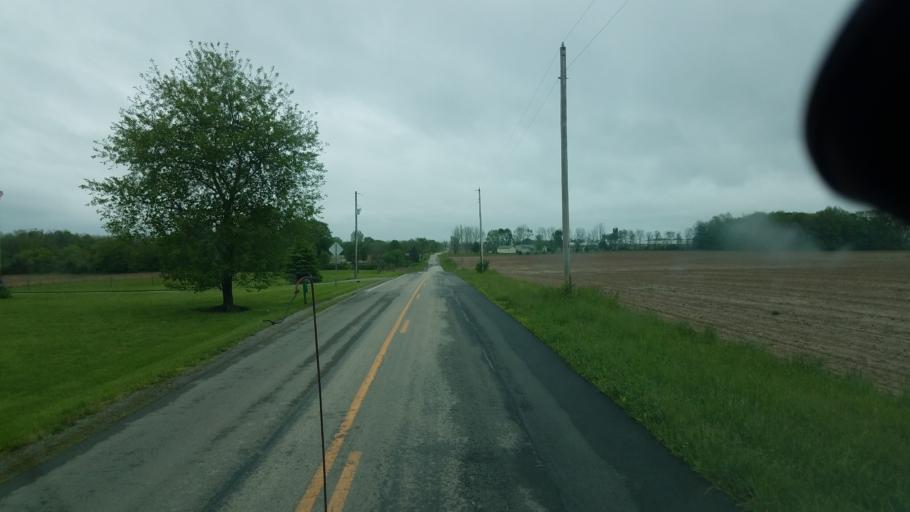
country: US
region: Ohio
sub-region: Highland County
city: Leesburg
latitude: 39.3311
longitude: -83.4988
